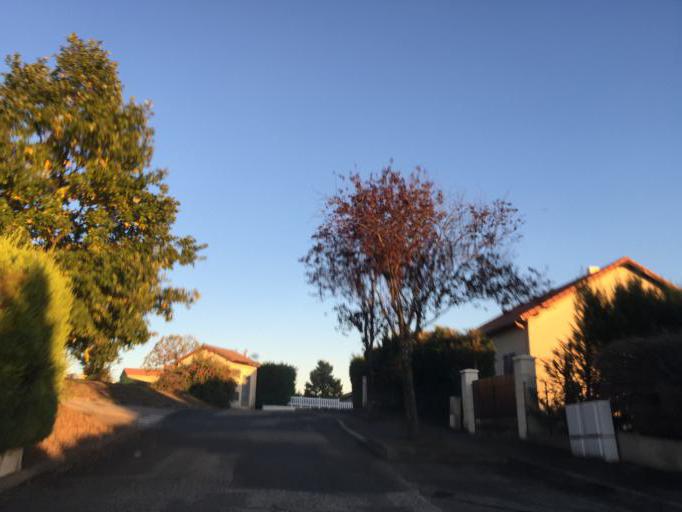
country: FR
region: Rhone-Alpes
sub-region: Departement de la Loire
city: Saint-Chamond
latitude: 45.4880
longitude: 4.5305
